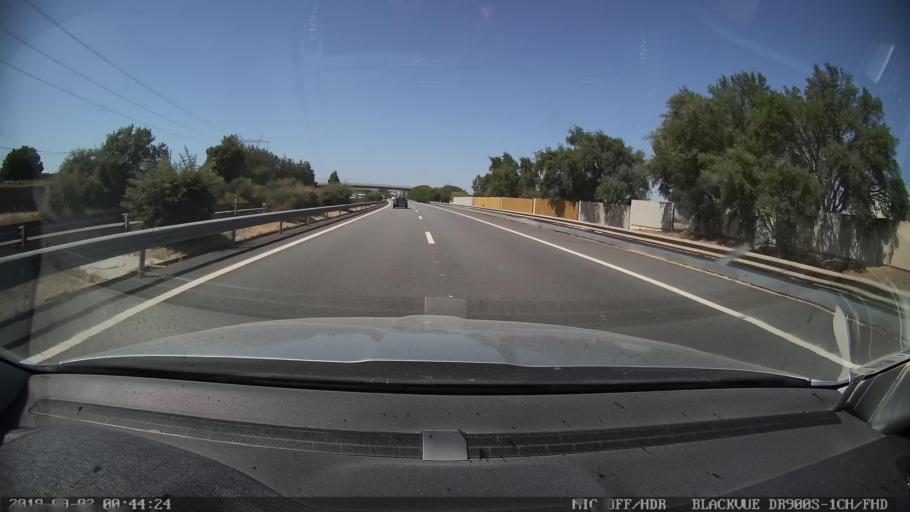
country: PT
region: Setubal
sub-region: Palmela
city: Palmela
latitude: 38.5866
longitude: -8.7813
